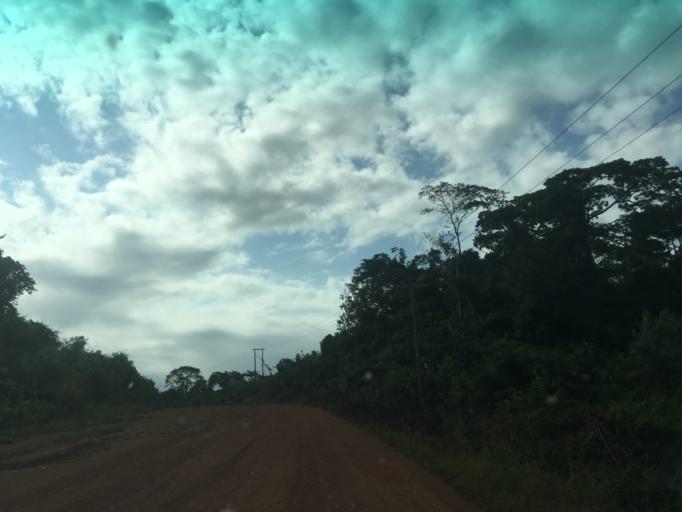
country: GH
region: Western
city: Wassa-Akropong
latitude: 5.9252
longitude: -2.4078
